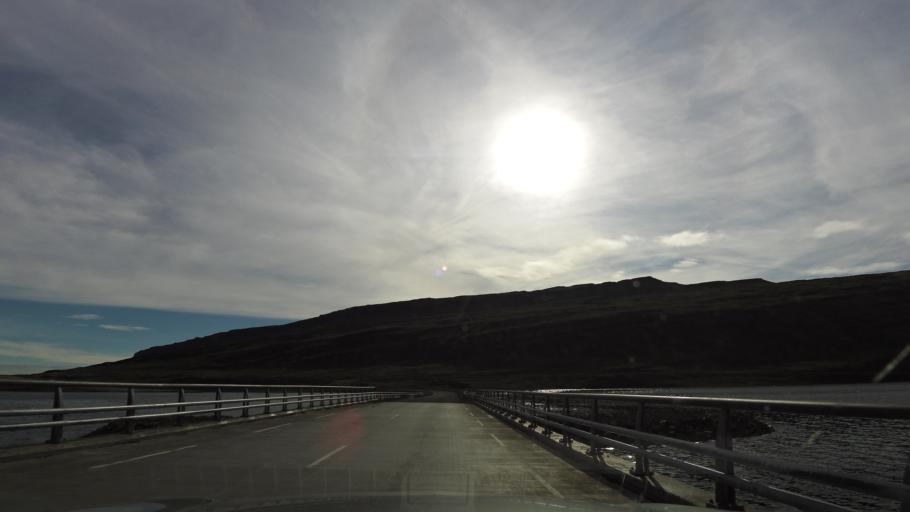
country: IS
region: West
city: Stykkisholmur
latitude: 65.6069
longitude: -22.8335
